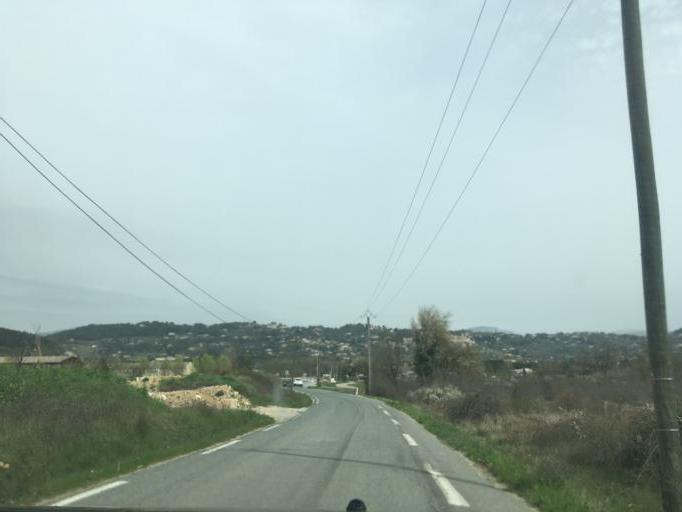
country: FR
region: Provence-Alpes-Cote d'Azur
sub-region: Departement du Var
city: Callian
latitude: 43.6056
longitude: 6.7419
